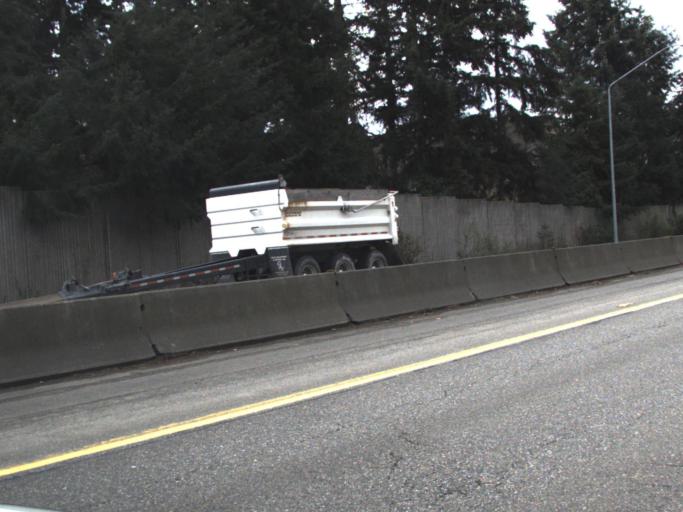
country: US
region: Washington
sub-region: King County
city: Covington
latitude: 47.3635
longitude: -122.1119
